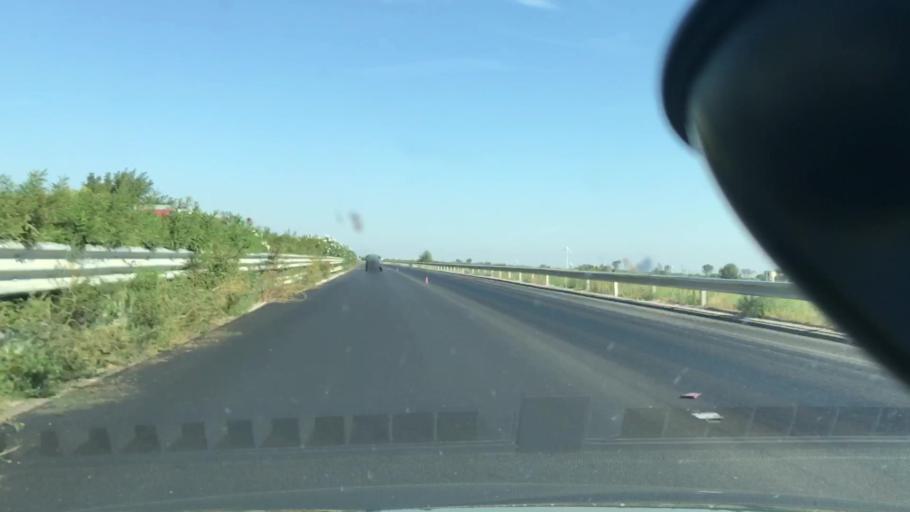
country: IT
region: Apulia
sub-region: Provincia di Foggia
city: Ascoli Satriano
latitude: 41.2758
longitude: 15.5535
